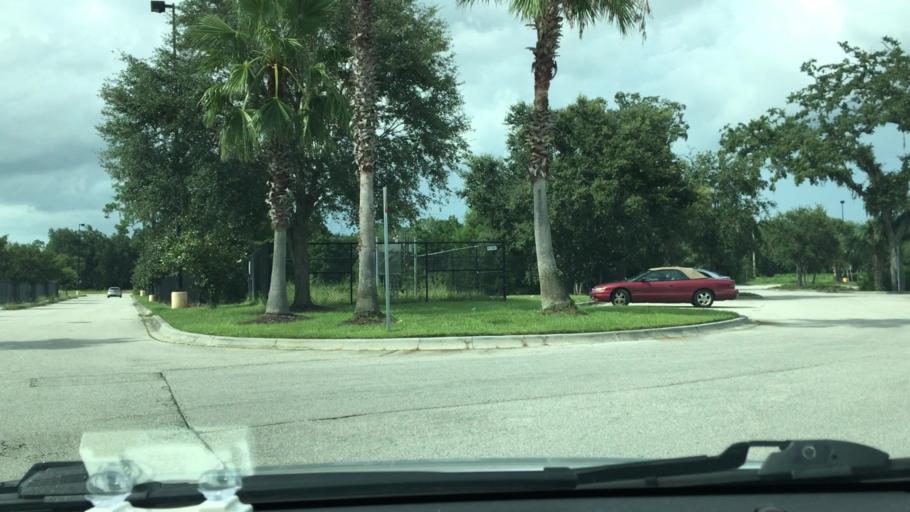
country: US
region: Florida
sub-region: Seminole County
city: Lake Mary
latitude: 28.8036
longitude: -81.3301
